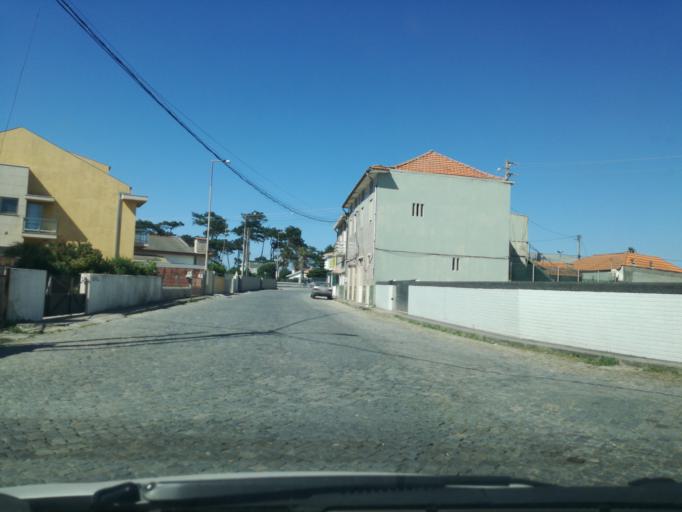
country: PT
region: Porto
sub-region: Matosinhos
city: Lavra
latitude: 41.2663
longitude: -8.7221
